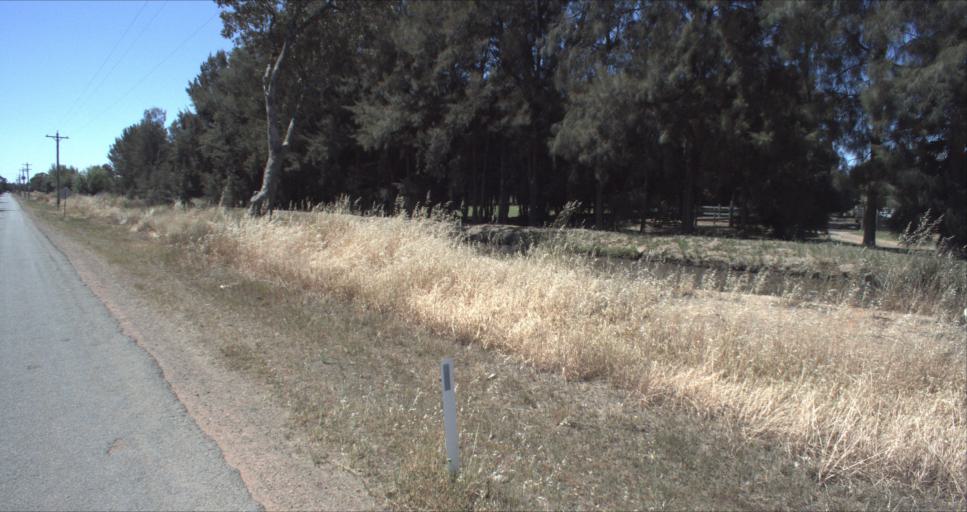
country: AU
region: New South Wales
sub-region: Leeton
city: Leeton
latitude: -34.5303
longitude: 146.3292
